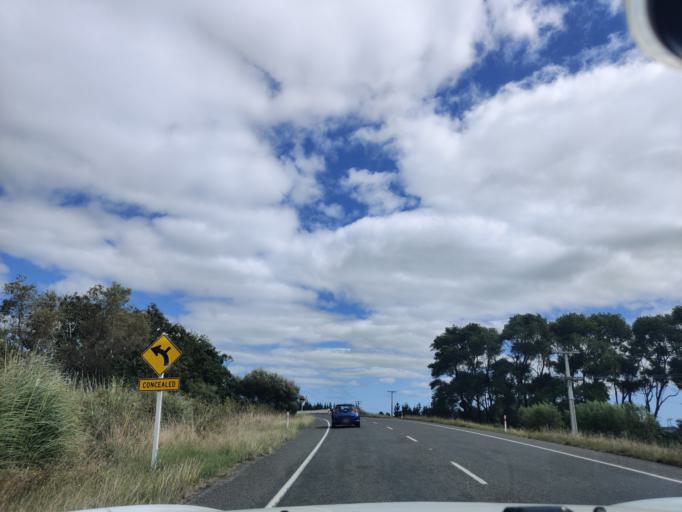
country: NZ
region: Manawatu-Wanganui
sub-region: Horowhenua District
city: Foxton
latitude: -40.4229
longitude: 175.4478
